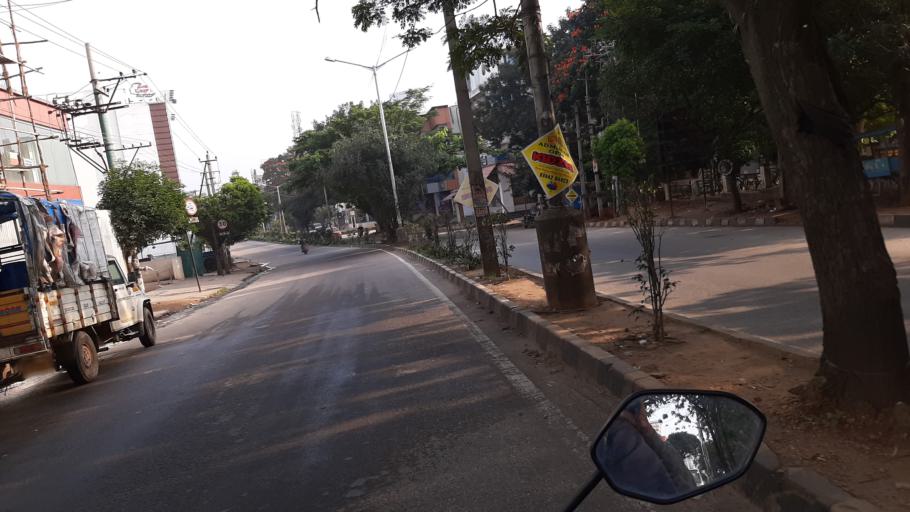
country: IN
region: Karnataka
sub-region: Bangalore Urban
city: Bangalore
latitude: 12.9801
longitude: 77.5108
